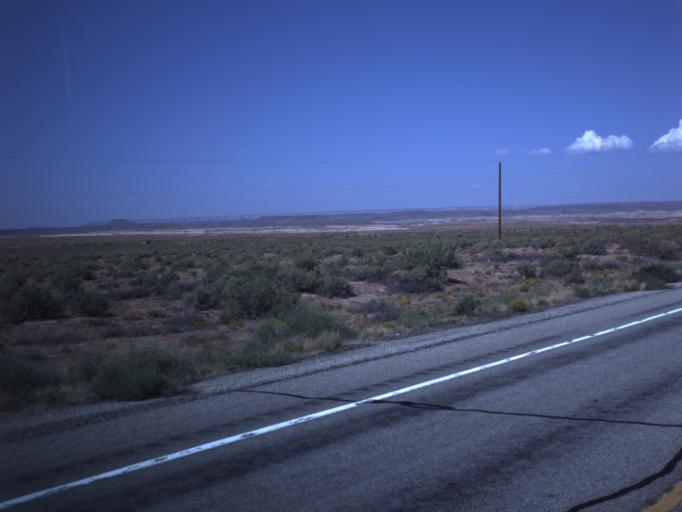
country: US
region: Utah
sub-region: San Juan County
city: Blanding
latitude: 37.1952
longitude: -109.5995
